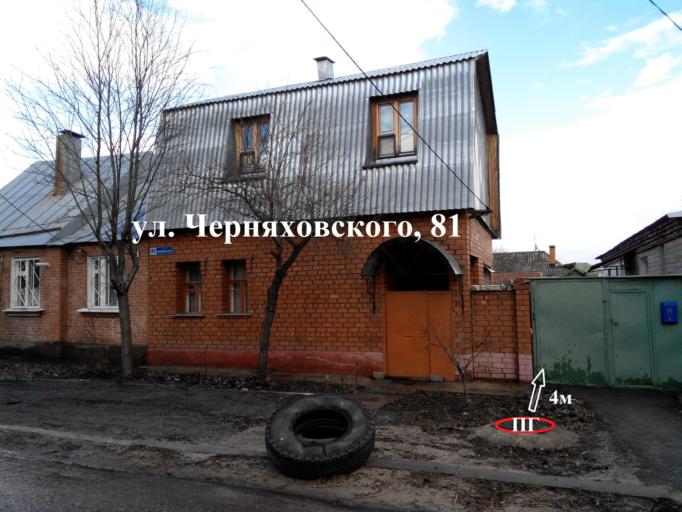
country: RU
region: Voronezj
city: Voronezh
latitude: 51.6386
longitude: 39.1612
